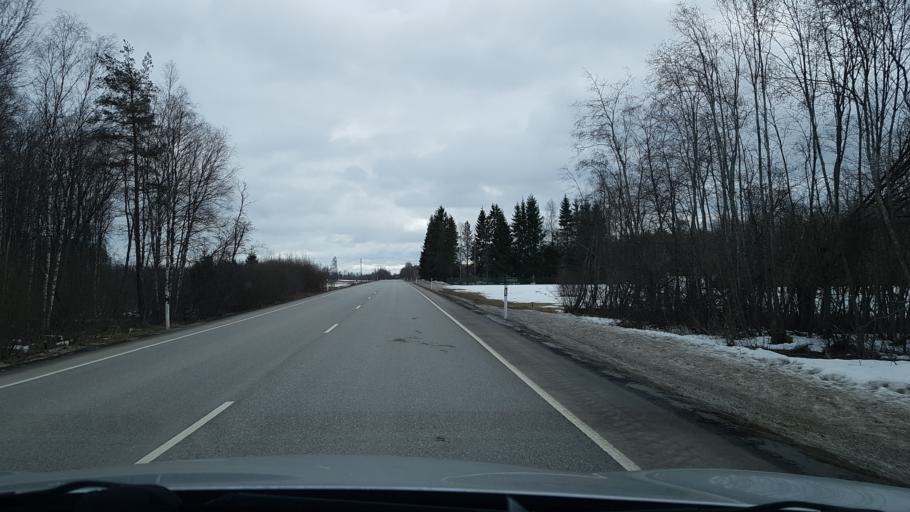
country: EE
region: Jogevamaa
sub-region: Tabivere vald
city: Tabivere
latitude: 58.6169
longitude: 26.5758
